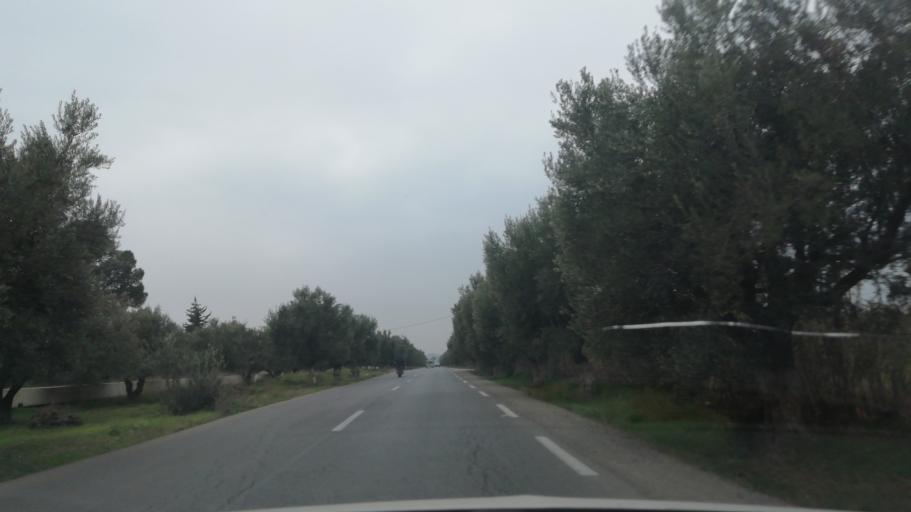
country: DZ
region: Sidi Bel Abbes
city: Sfizef
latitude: 35.2168
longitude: -0.3063
